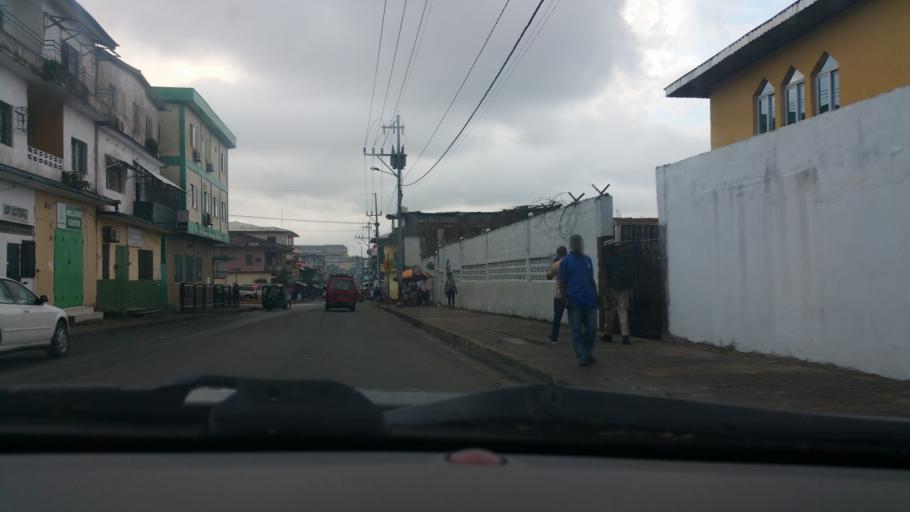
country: LR
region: Montserrado
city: Monrovia
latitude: 6.3107
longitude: -10.8008
